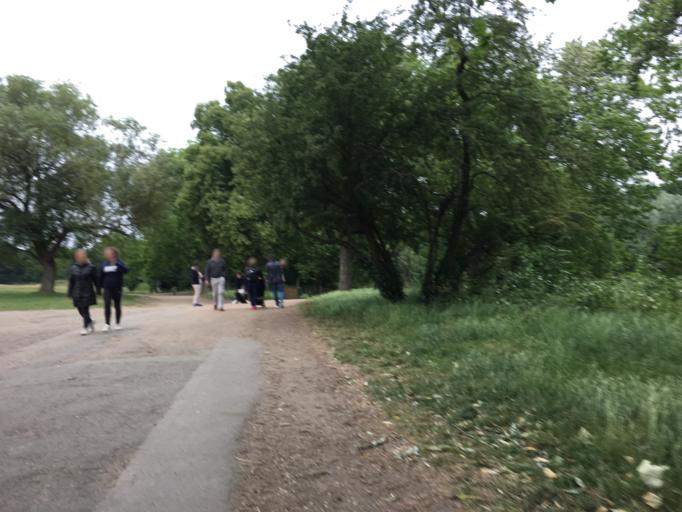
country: GB
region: England
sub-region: Greater London
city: Belsize Park
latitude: 51.5588
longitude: -0.1664
